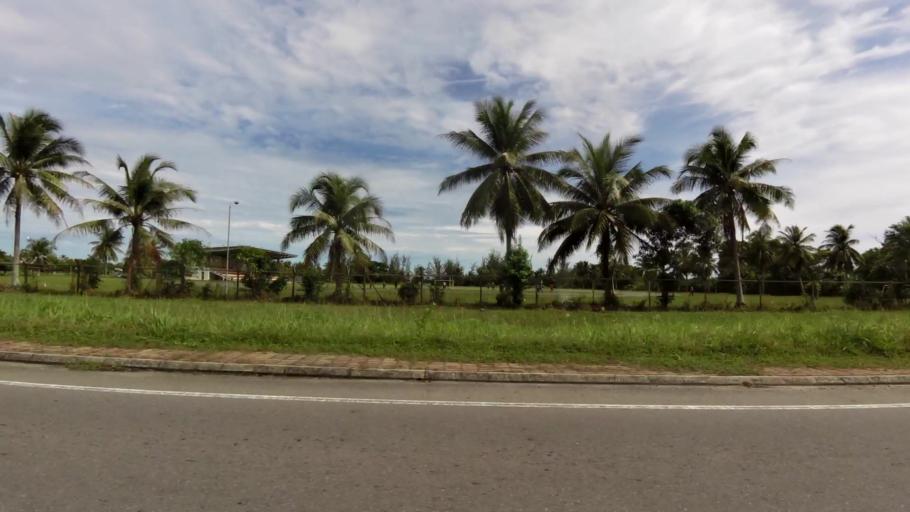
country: BN
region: Belait
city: Seria
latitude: 4.6160
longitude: 114.3306
